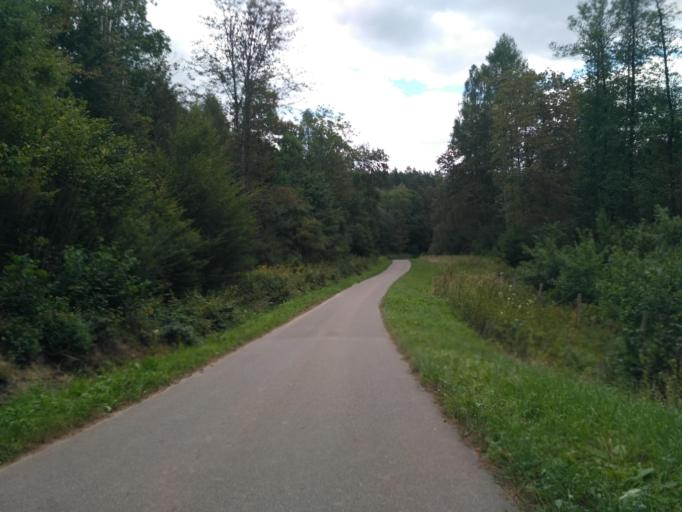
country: PL
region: Subcarpathian Voivodeship
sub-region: Powiat rzeszowski
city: Dynow
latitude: 49.7629
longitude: 22.2767
